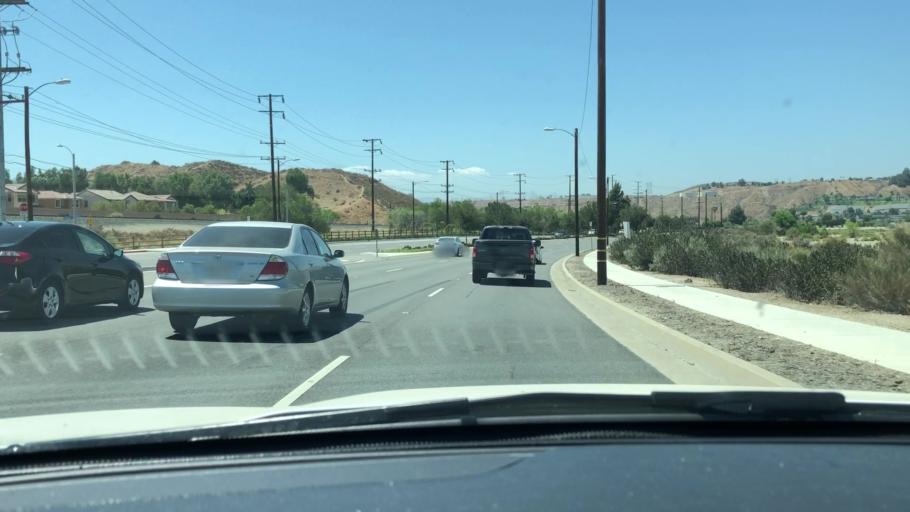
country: US
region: California
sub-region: Los Angeles County
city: Santa Clarita
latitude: 34.4169
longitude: -118.4804
